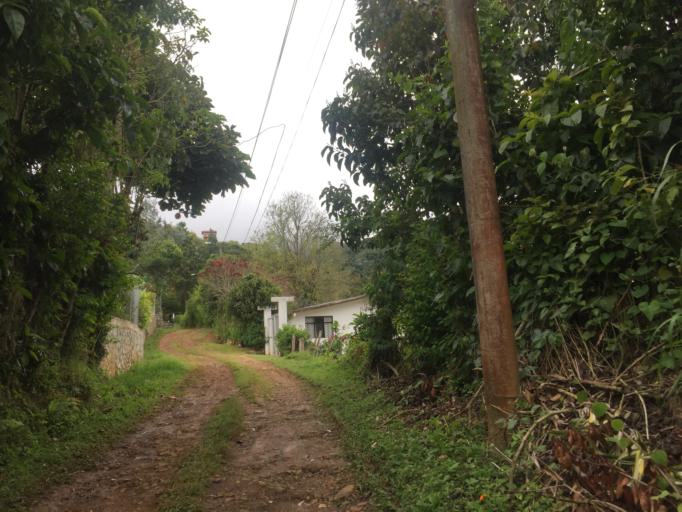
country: CO
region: Valle del Cauca
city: Cali
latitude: 3.4629
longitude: -76.6343
